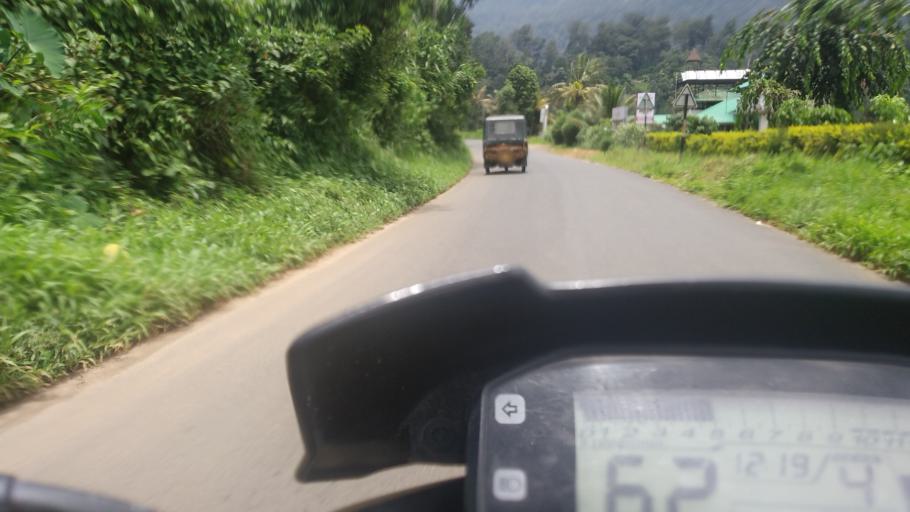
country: IN
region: Kerala
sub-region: Idukki
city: Munnar
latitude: 10.0213
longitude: 77.0034
